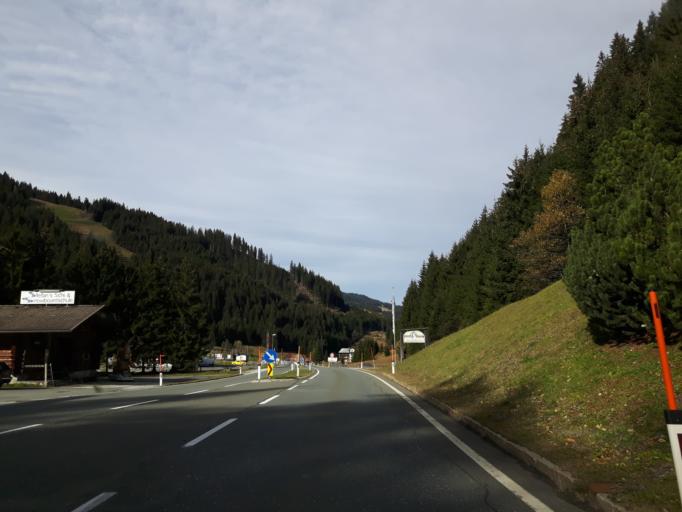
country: AT
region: Salzburg
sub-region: Politischer Bezirk Zell am See
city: Hollersbach im Pinzgau
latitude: 47.3135
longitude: 12.4076
